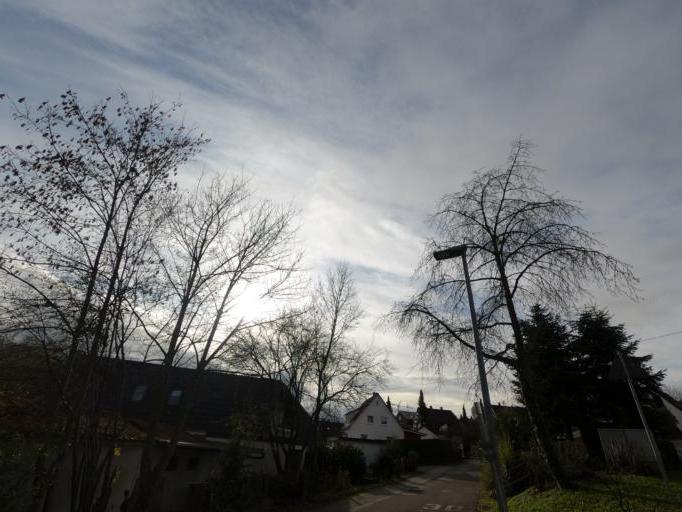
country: DE
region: Baden-Wuerttemberg
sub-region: Regierungsbezirk Stuttgart
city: Albershausen
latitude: 48.6994
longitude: 9.5696
